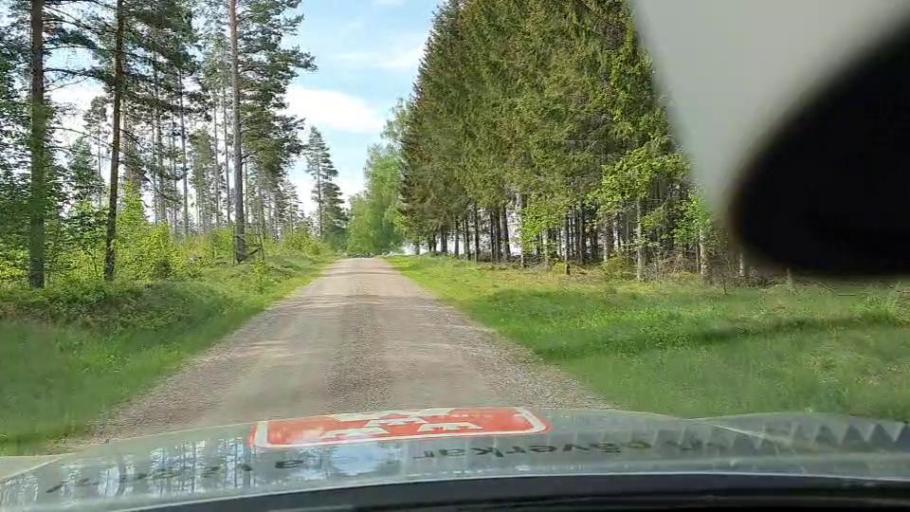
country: SE
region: Soedermanland
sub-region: Strangnas Kommun
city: Akers Styckebruk
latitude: 59.2472
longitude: 16.9336
